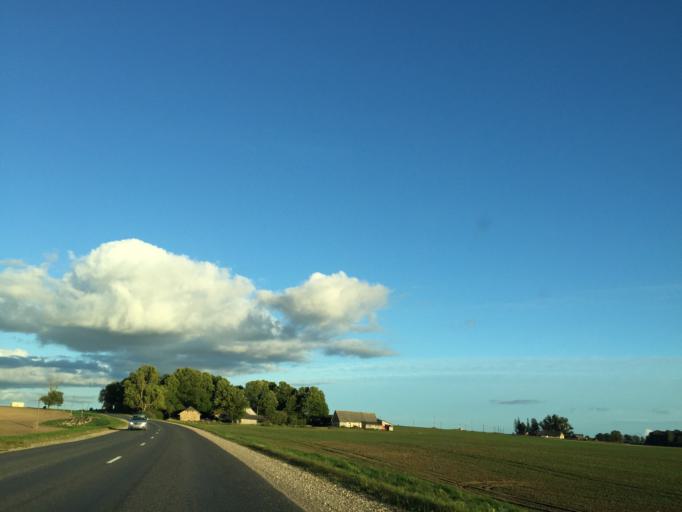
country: LV
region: Saldus Rajons
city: Saldus
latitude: 56.7138
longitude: 22.4004
